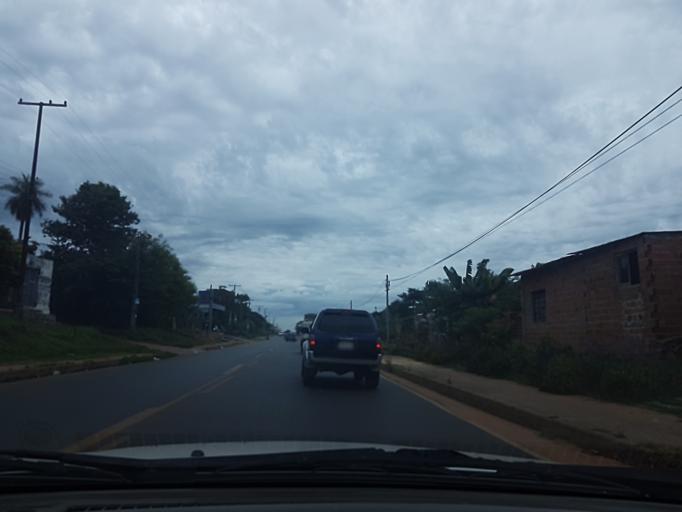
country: PY
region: Central
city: Limpio
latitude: -25.2540
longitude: -57.4693
